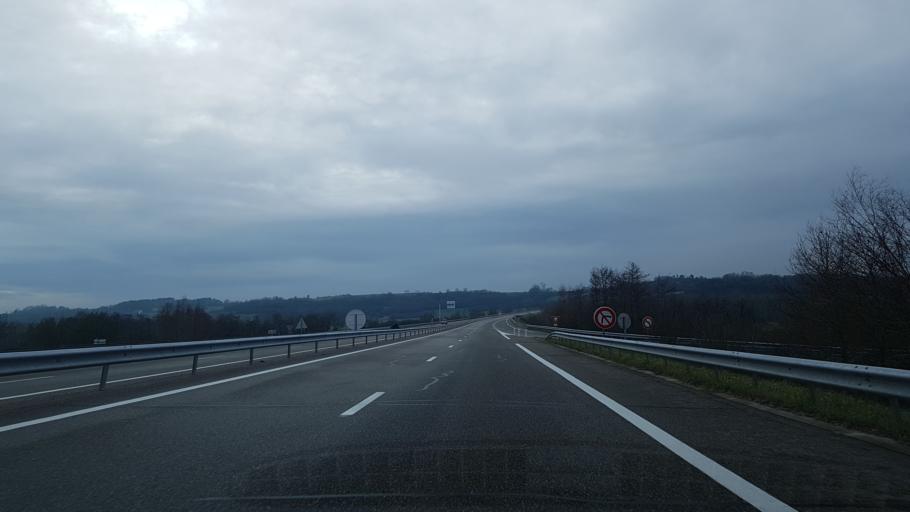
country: FR
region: Lorraine
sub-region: Departement de la Moselle
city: Petit-Rederching
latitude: 49.0914
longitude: 7.2776
